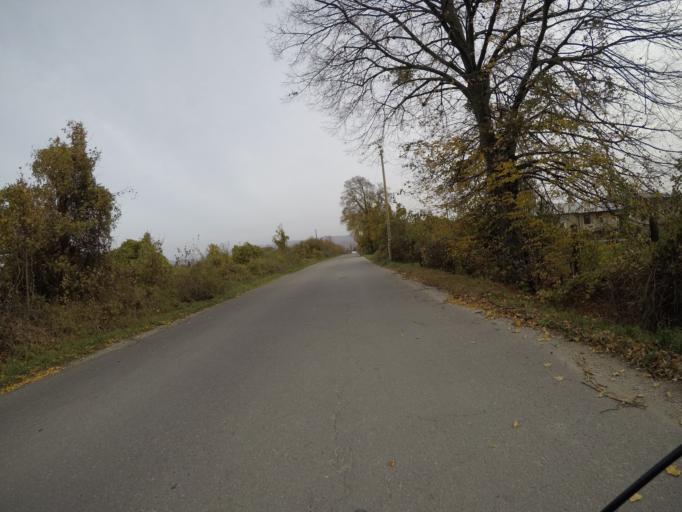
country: SK
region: Trenciansky
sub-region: Okres Nove Mesto nad Vahom
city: Nove Mesto nad Vahom
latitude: 48.7432
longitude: 17.8150
